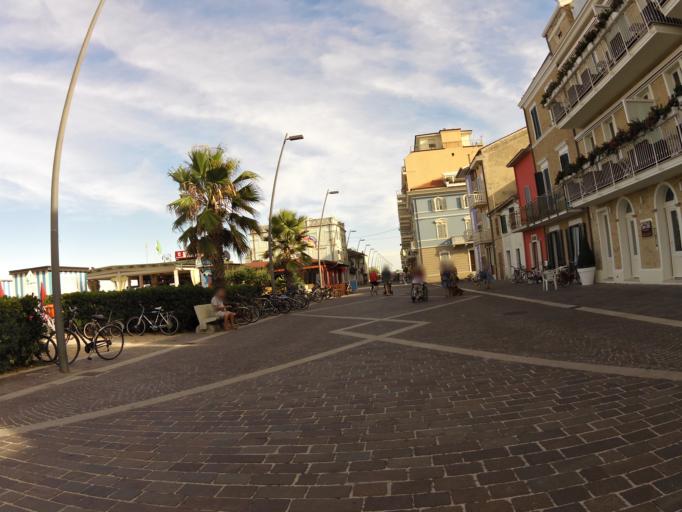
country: IT
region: The Marches
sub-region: Provincia di Macerata
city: Porto Recanati
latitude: 43.4310
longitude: 13.6665
